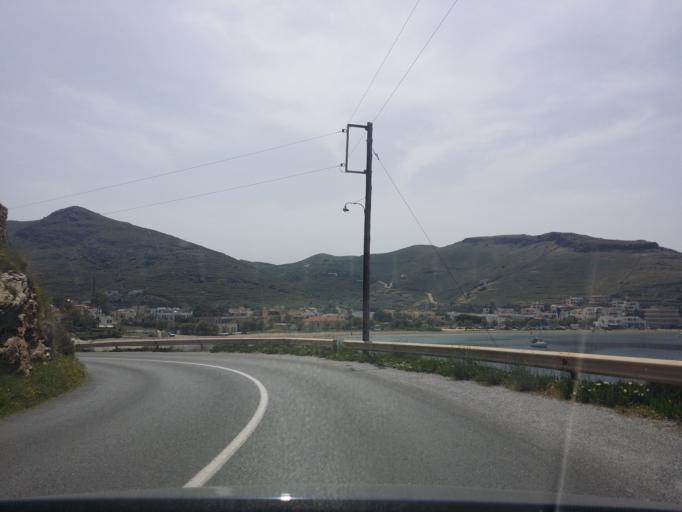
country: GR
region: South Aegean
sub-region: Nomos Kykladon
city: Kea
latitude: 37.6602
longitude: 24.3175
